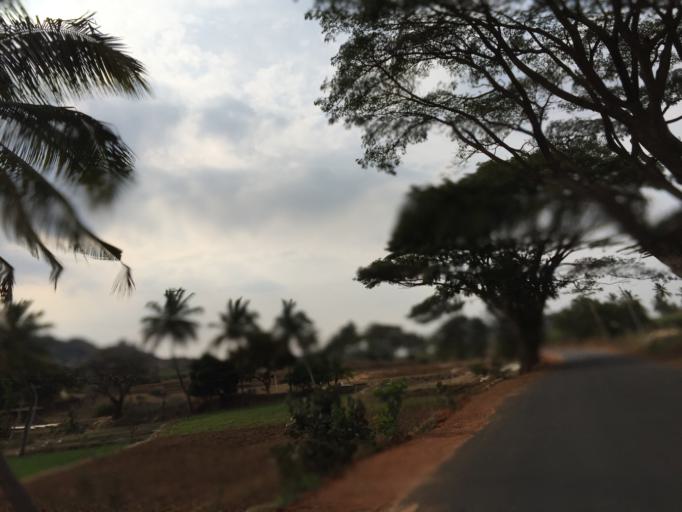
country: IN
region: Karnataka
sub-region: Chikkaballapur
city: Chik Ballapur
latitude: 13.5535
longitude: 77.7448
